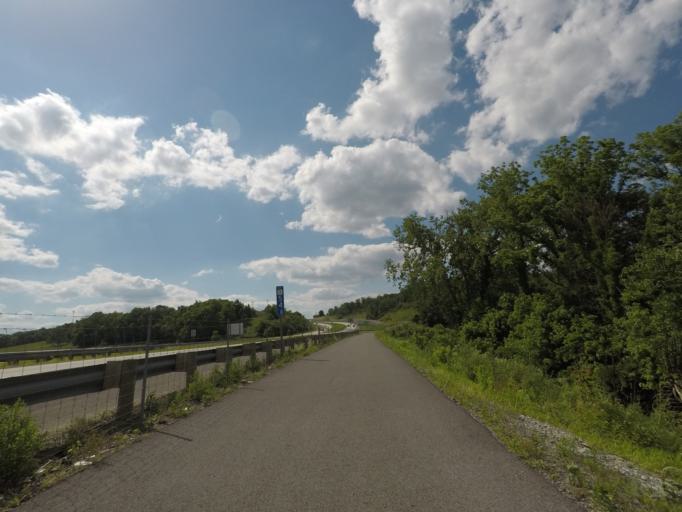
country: US
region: West Virginia
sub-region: Berkeley County
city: Martinsburg
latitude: 39.4255
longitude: -77.9388
